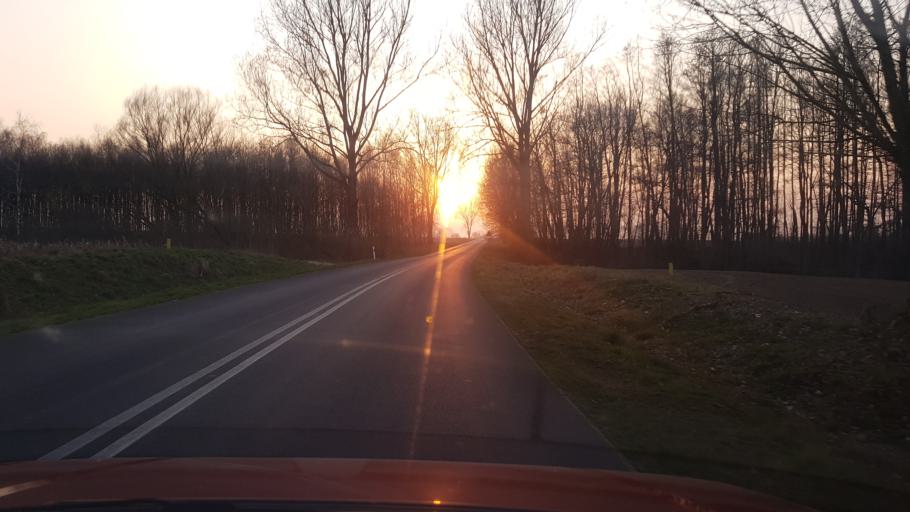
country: PL
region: West Pomeranian Voivodeship
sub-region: Powiat lobeski
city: Radowo Male
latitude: 53.6642
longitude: 15.4686
